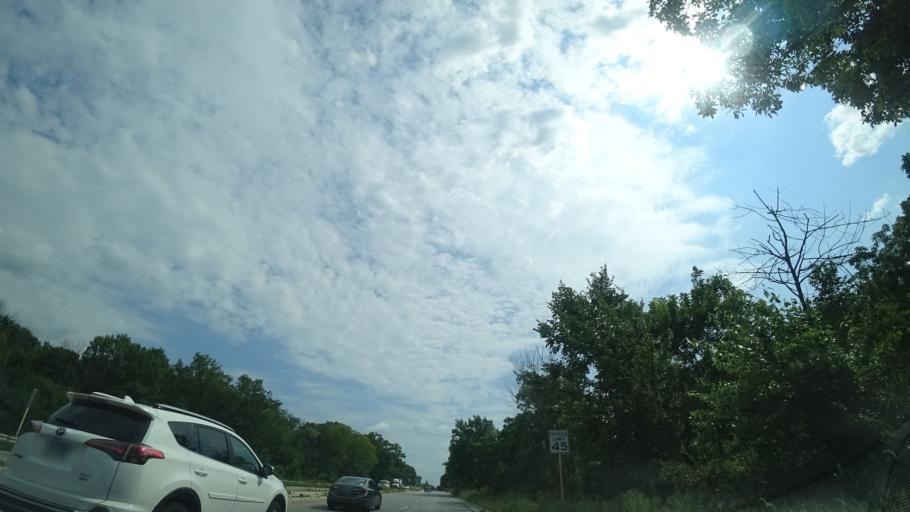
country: US
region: Illinois
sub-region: Cook County
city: Palos Heights
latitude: 41.6507
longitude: -87.7959
